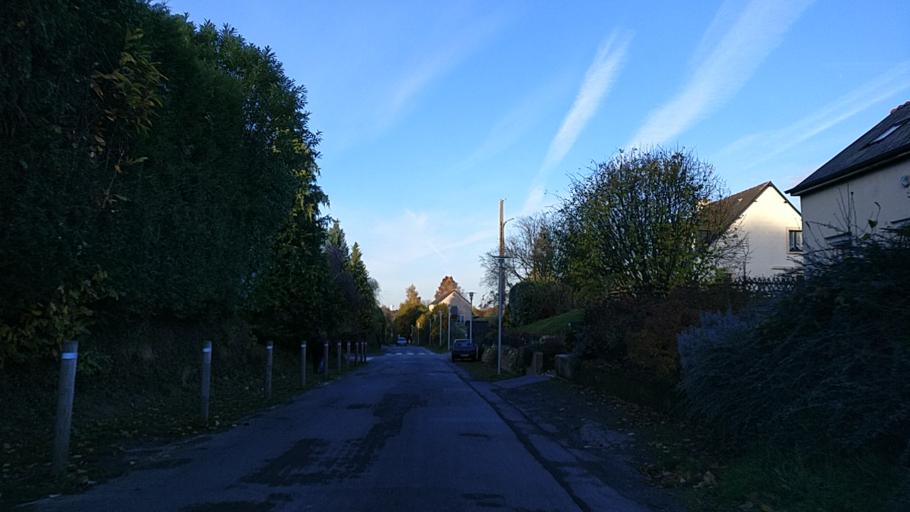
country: FR
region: Brittany
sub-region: Departement d'Ille-et-Vilaine
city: Saint-Sulpice-la-Foret
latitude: 48.2130
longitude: -1.5793
